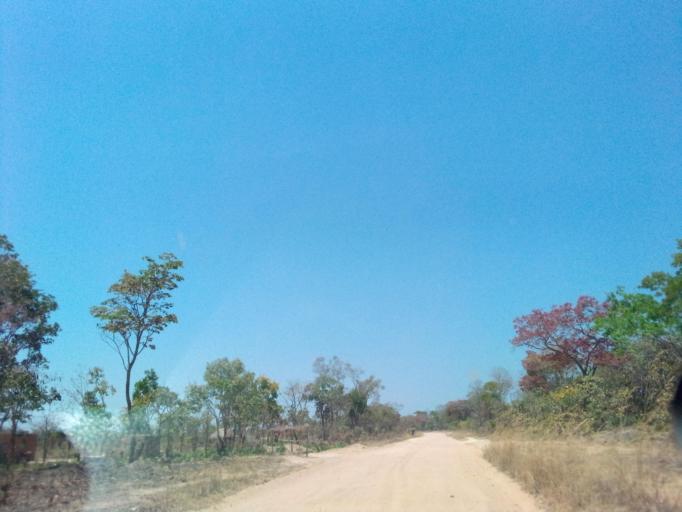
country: ZM
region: Northern
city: Mpika
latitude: -12.2313
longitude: 30.6574
